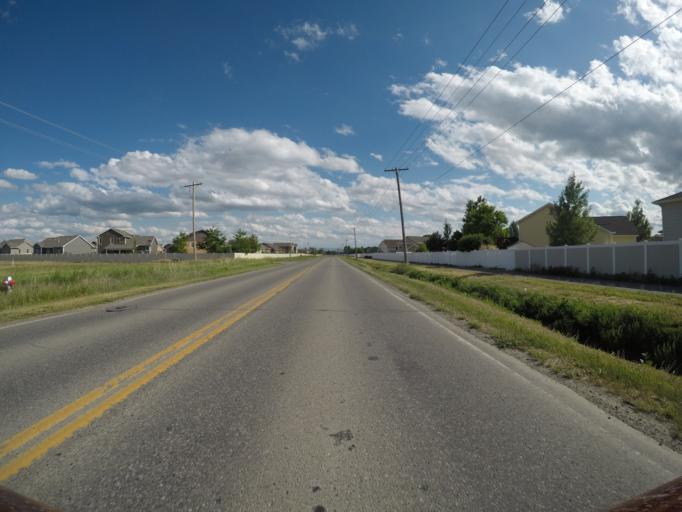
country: US
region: Montana
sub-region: Yellowstone County
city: Billings
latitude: 45.7900
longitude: -108.6527
